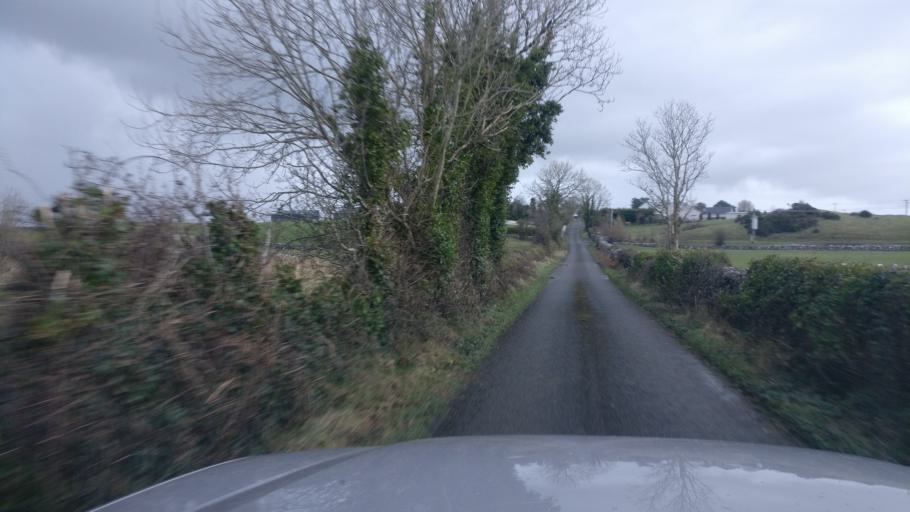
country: IE
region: Connaught
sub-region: County Galway
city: Loughrea
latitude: 53.1770
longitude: -8.6889
